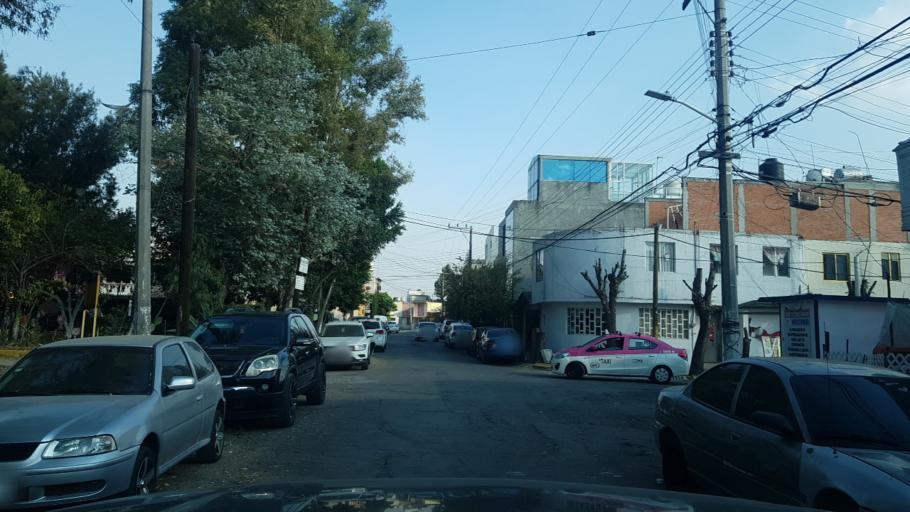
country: MX
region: Mexico
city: Santiago Teyahualco
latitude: 19.6529
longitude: -99.1172
